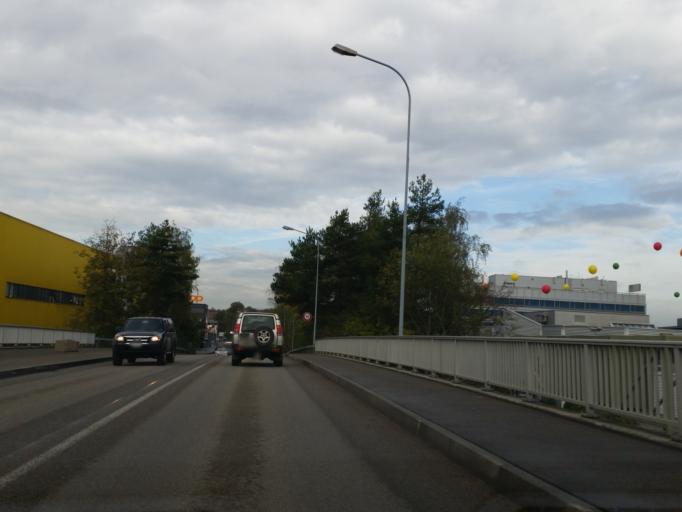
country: CH
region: Zurich
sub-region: Bezirk Buelach
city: Dietlikon / Dietlikon (Dorf)
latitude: 47.4122
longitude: 8.6214
